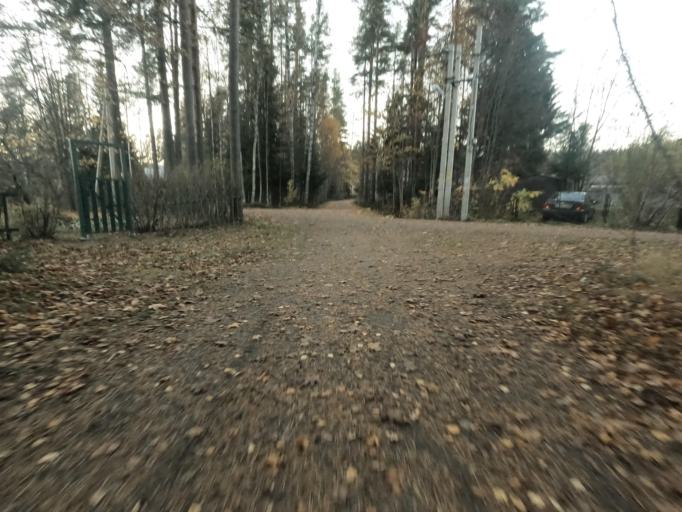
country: RU
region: St.-Petersburg
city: Komarovo
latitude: 60.2002
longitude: 29.8251
